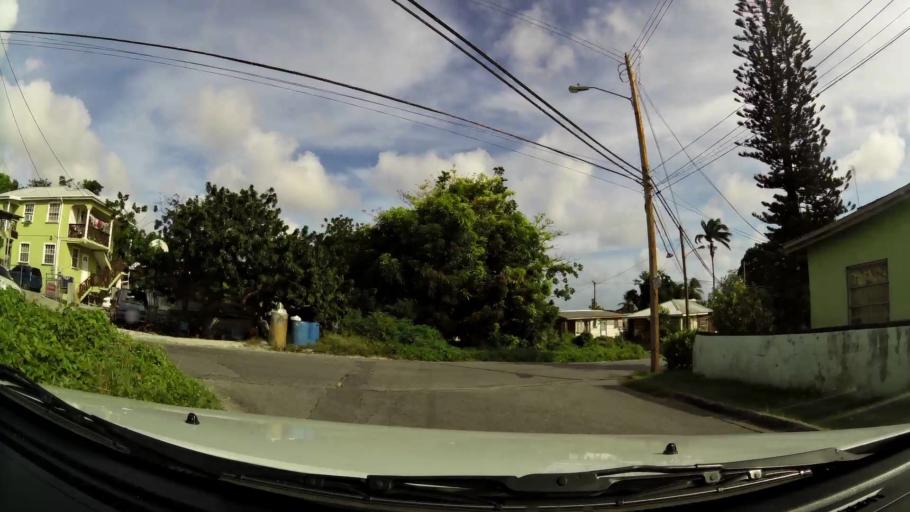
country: BB
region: Saint Michael
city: Bridgetown
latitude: 13.0868
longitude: -59.5886
